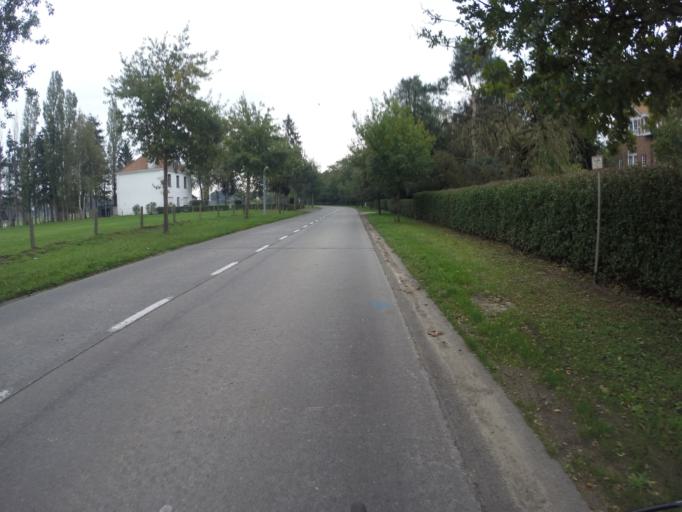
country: BE
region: Flanders
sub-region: Provincie West-Vlaanderen
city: Beernem
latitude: 51.0853
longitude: 3.3444
